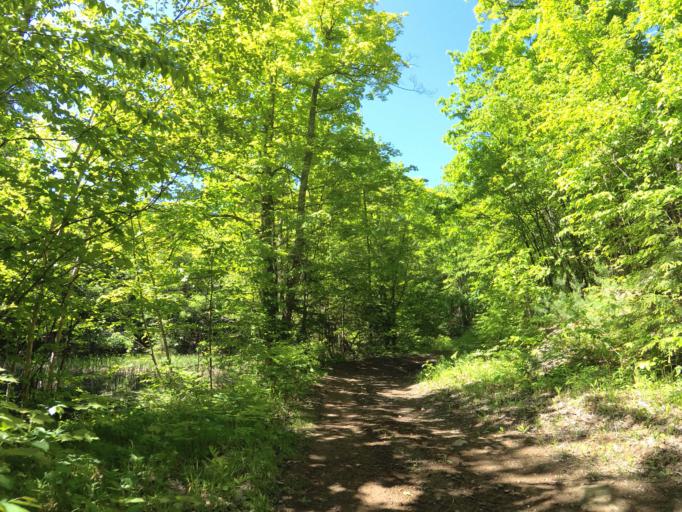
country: CA
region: Ontario
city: Renfrew
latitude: 45.0521
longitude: -77.0884
